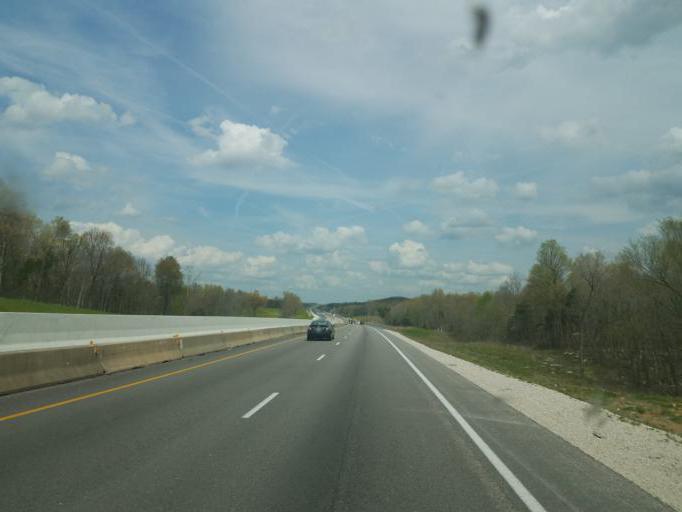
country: US
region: Kentucky
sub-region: Hart County
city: Munfordville
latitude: 37.4050
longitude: -85.8813
